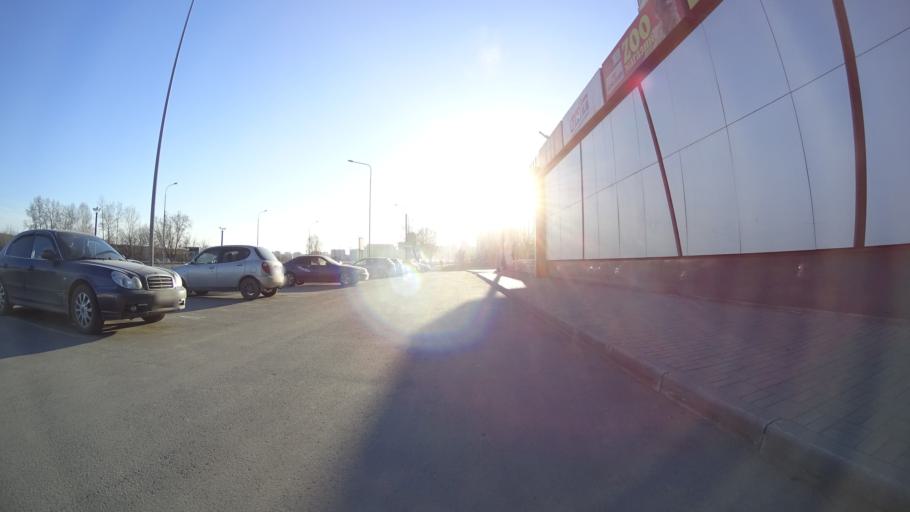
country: RU
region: Chelyabinsk
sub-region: Gorod Chelyabinsk
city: Chelyabinsk
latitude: 55.1746
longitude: 61.3400
